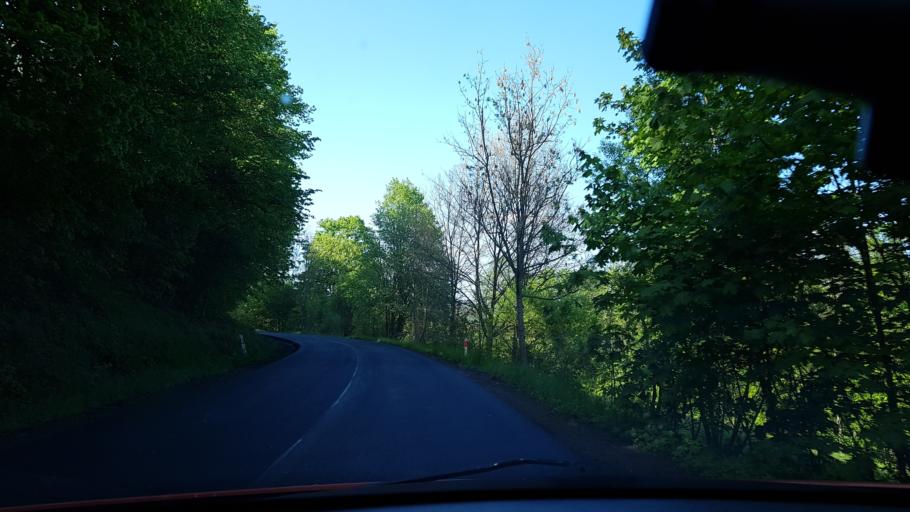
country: PL
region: Lower Silesian Voivodeship
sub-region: Powiat klodzki
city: Nowa Ruda
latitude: 50.5510
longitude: 16.4663
